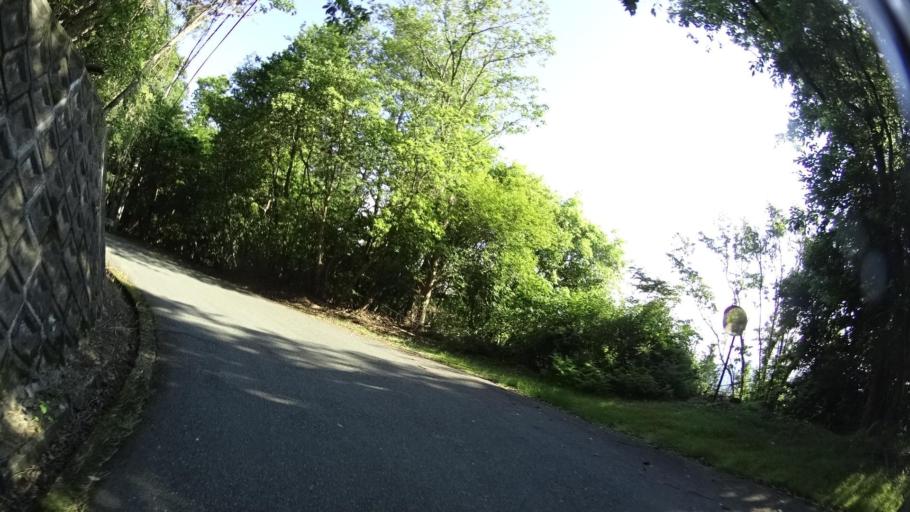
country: JP
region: Kyoto
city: Kameoka
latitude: 34.9822
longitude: 135.5562
